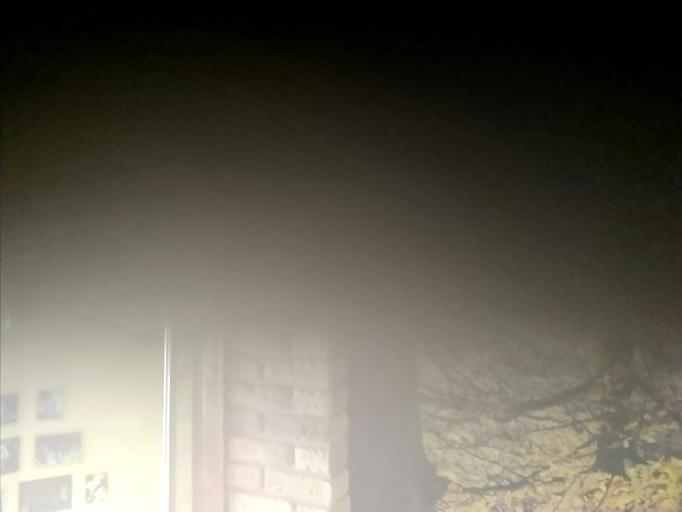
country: RU
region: Kaluga
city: Yukhnov
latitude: 54.6654
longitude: 35.0648
